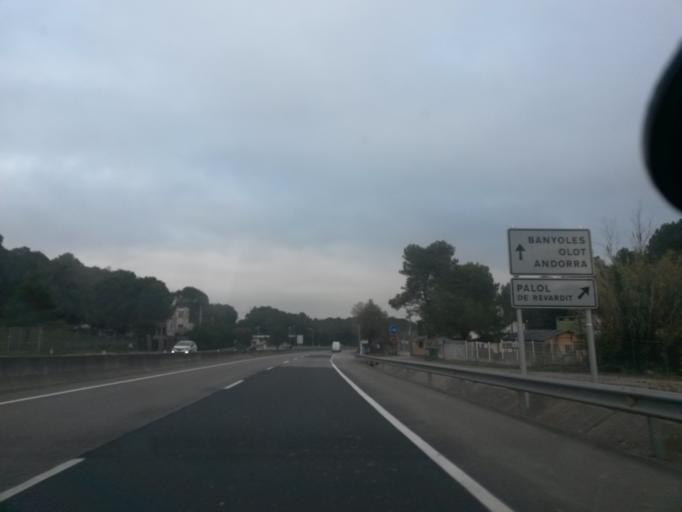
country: ES
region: Catalonia
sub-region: Provincia de Girona
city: Palol de Revardit
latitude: 42.0612
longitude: 2.8128
